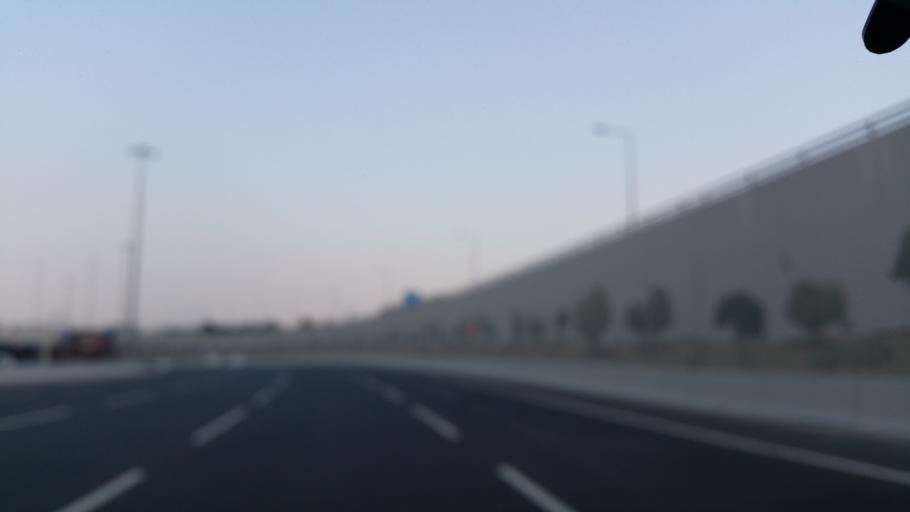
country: QA
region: Baladiyat ar Rayyan
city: Ar Rayyan
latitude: 25.3015
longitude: 51.4522
